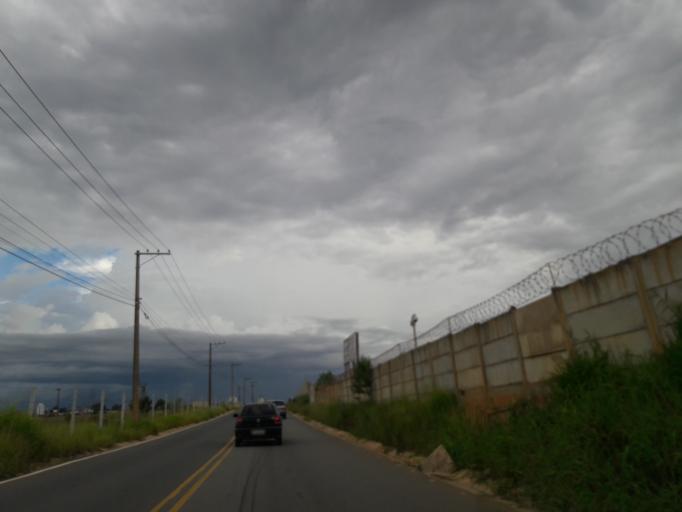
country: BR
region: Sao Paulo
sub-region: Aruja
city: Aruja
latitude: -23.3932
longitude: -46.4095
